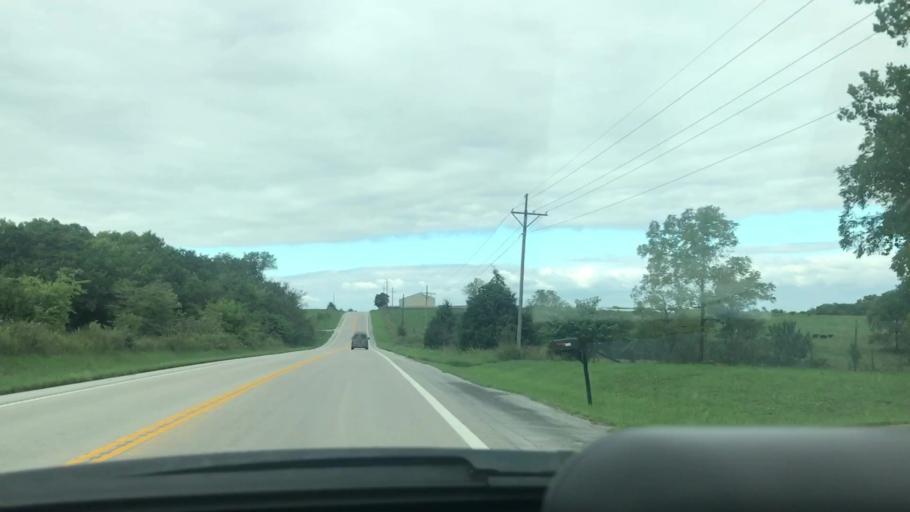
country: US
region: Missouri
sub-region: Hickory County
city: Hermitage
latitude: 37.8804
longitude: -93.1802
